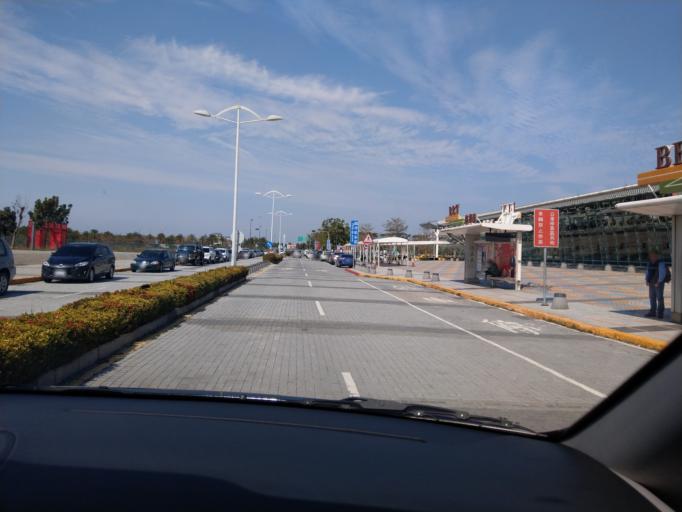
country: TW
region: Taiwan
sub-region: Chiayi
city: Taibao
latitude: 23.4589
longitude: 120.3226
